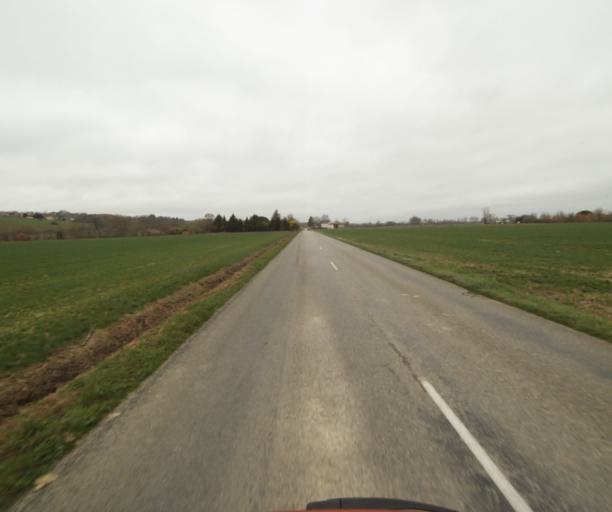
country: FR
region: Midi-Pyrenees
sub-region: Departement de la Haute-Garonne
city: Cintegabelle
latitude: 43.2623
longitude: 1.5266
